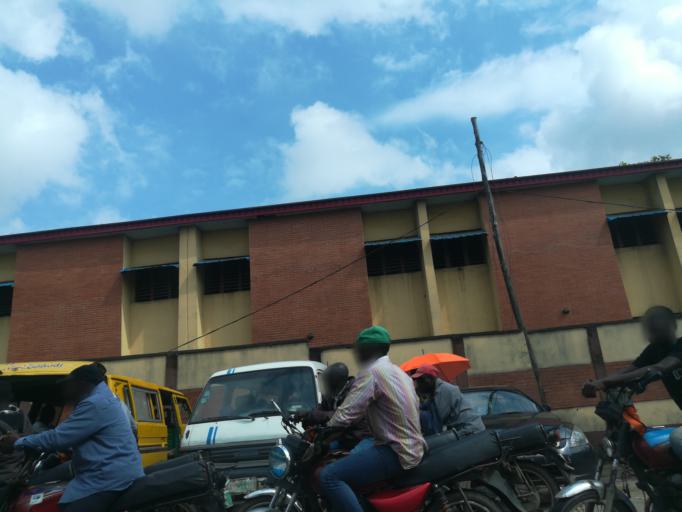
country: NG
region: Lagos
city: Oshodi
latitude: 6.5553
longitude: 3.3535
